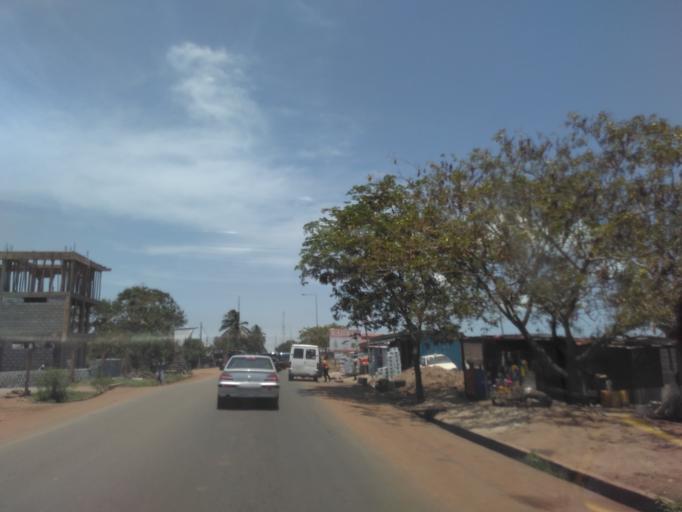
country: GH
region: Greater Accra
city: Tema
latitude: 5.6805
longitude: -0.0193
